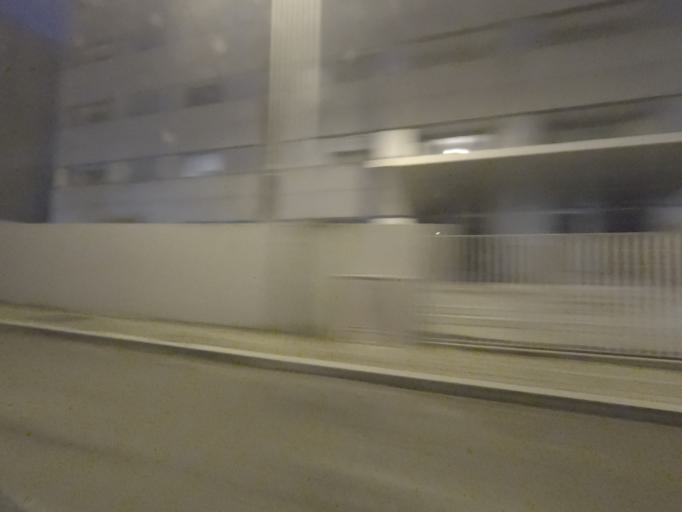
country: PT
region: Porto
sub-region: Matosinhos
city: Senhora da Hora
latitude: 41.1640
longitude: -8.6402
